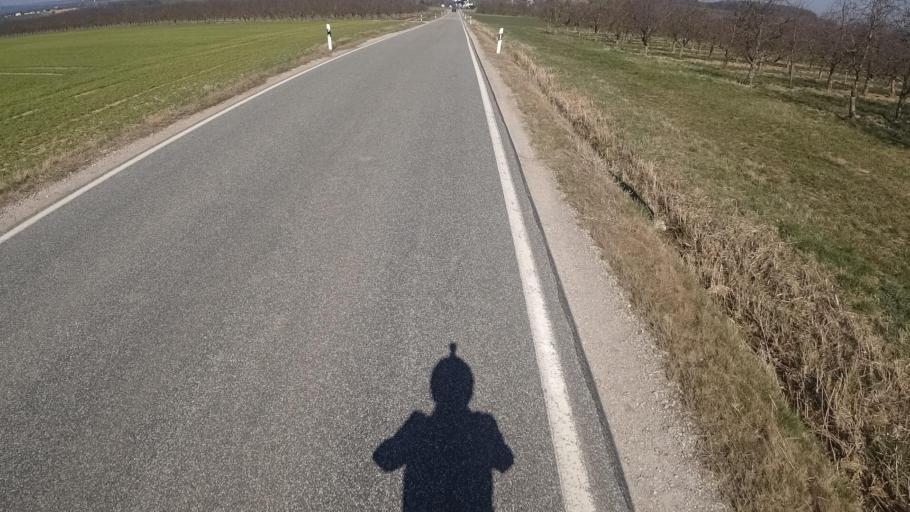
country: DE
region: Rheinland-Pfalz
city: Schnorbach
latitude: 49.9826
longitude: 7.6054
